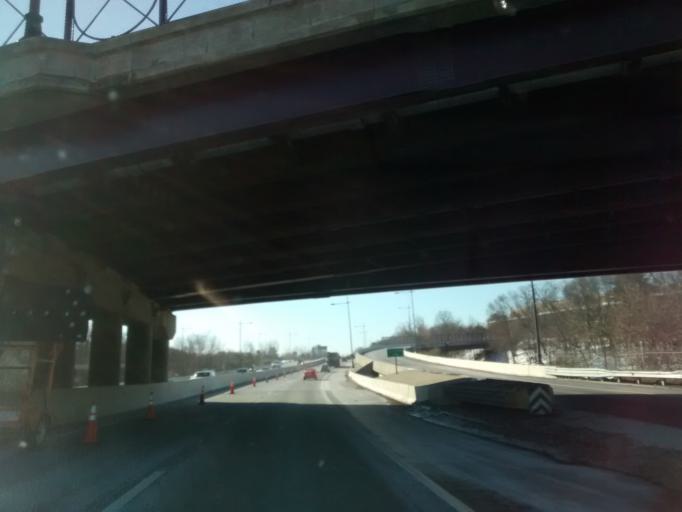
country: US
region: Massachusetts
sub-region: Worcester County
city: Millbury
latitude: 42.2022
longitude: -71.7762
